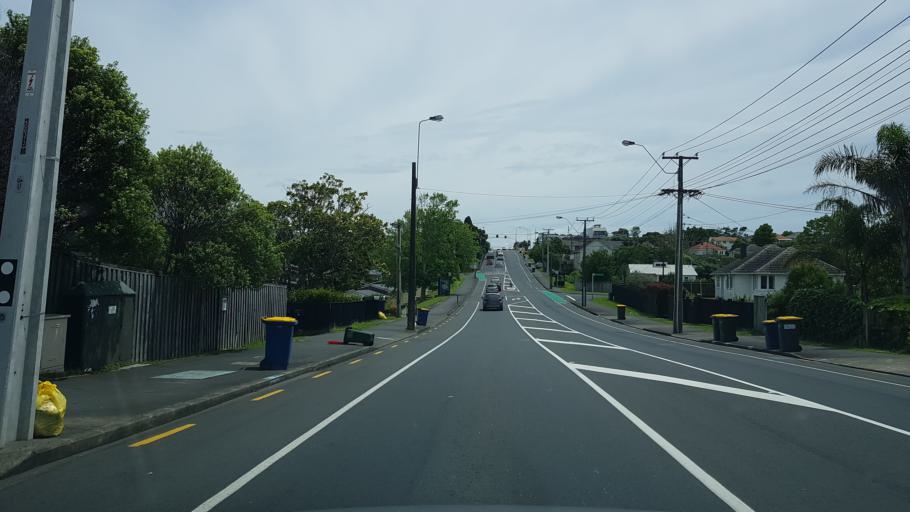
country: NZ
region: Auckland
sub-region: Auckland
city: North Shore
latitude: -36.8112
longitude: 174.7915
